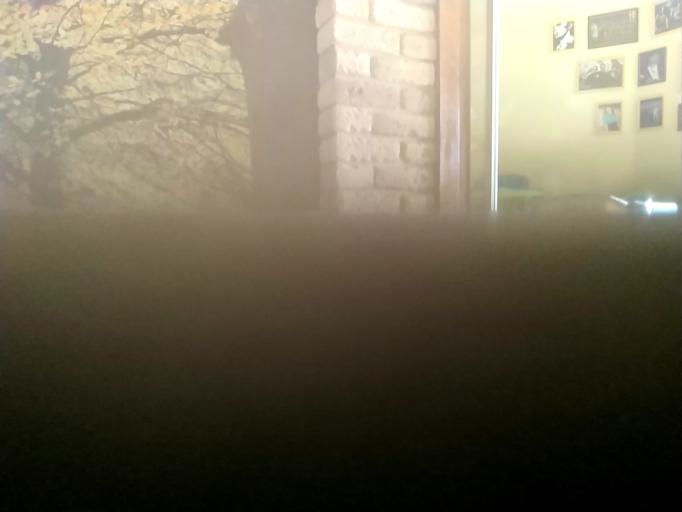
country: RU
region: Kaluga
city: Yukhnov
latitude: 54.7649
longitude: 35.0269
